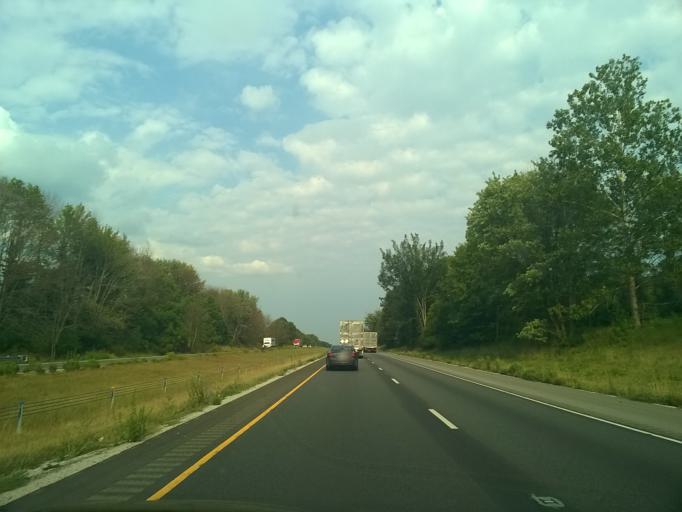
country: US
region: Indiana
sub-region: Clay County
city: Brazil
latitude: 39.4666
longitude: -87.0508
